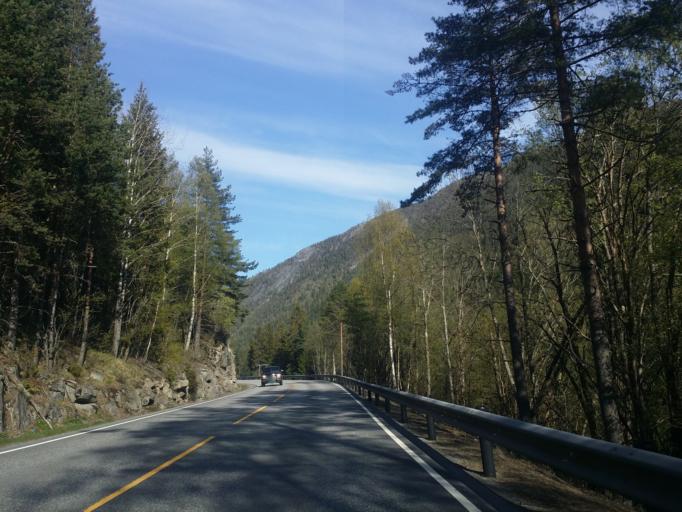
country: NO
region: Telemark
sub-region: Hjartdal
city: Sauland
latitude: 59.6100
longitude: 8.7791
